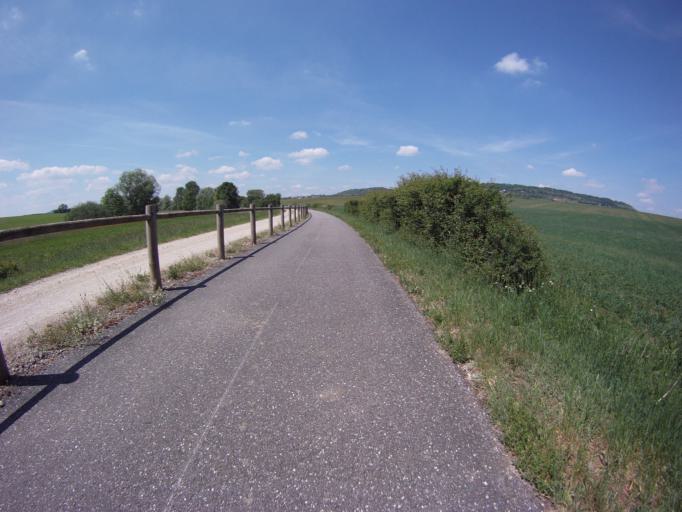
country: FR
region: Lorraine
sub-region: Departement de Meurthe-et-Moselle
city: Champenoux
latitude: 48.7417
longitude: 6.3034
